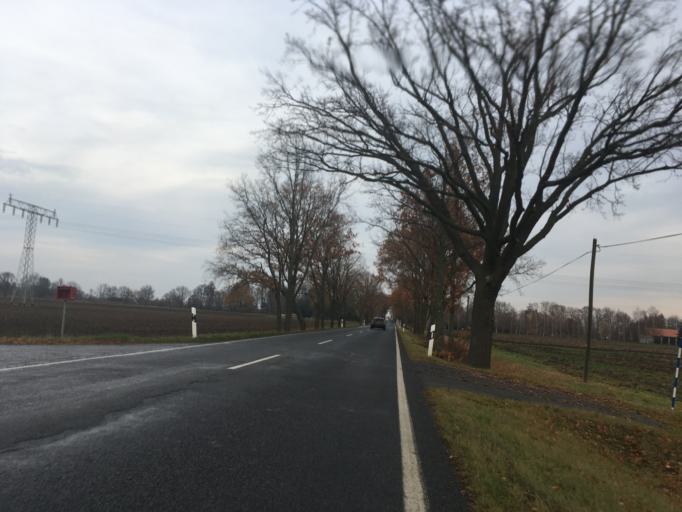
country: DE
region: Brandenburg
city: Letschin
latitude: 52.6256
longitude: 14.3508
